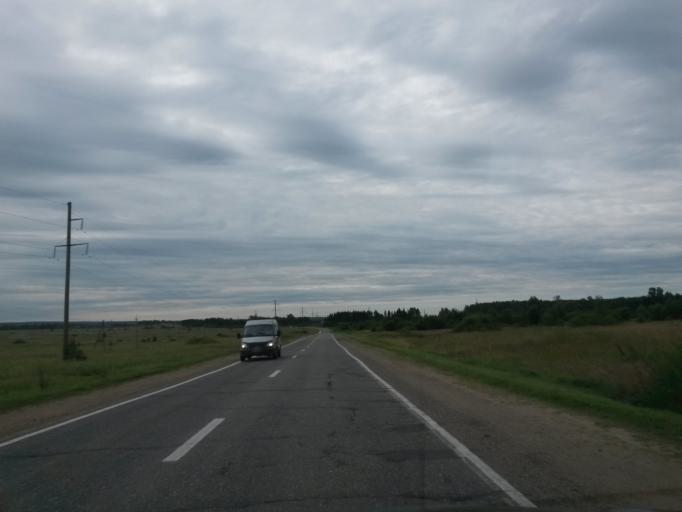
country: RU
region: Jaroslavl
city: Gavrilov-Yam
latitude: 57.3518
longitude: 39.7878
